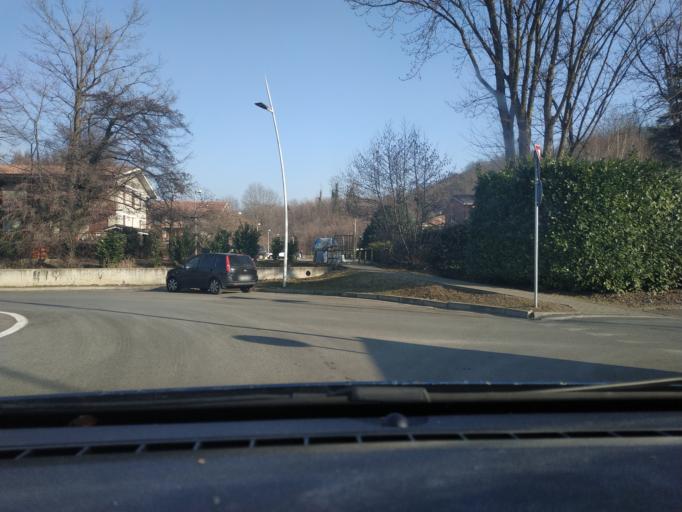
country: IT
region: Piedmont
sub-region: Provincia di Torino
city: Pavone Canavese
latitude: 45.4460
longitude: 7.8551
